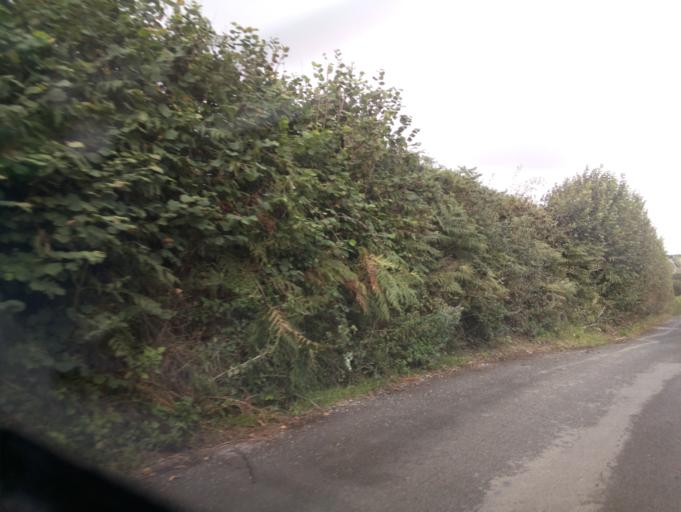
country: GB
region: England
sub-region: Devon
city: Dartmouth
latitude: 50.3335
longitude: -3.5866
